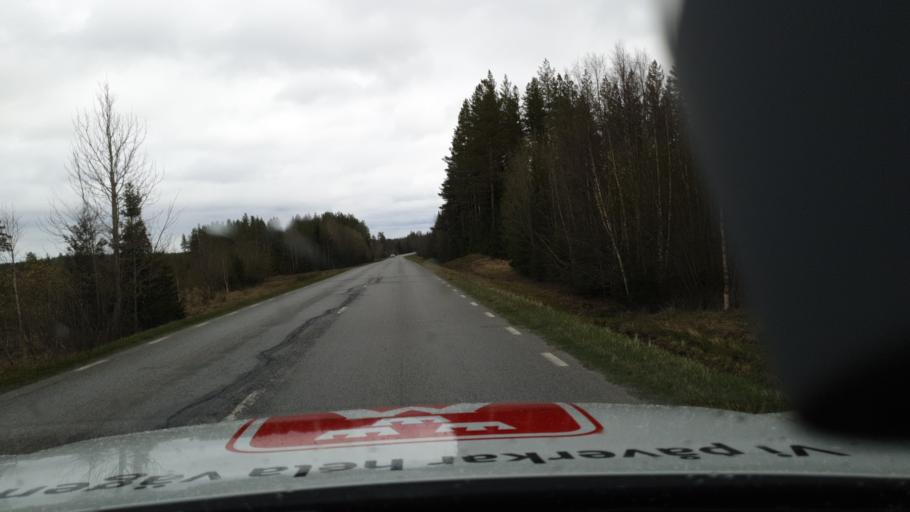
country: SE
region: Jaemtland
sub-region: Stroemsunds Kommun
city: Stroemsund
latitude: 63.6146
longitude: 15.2746
